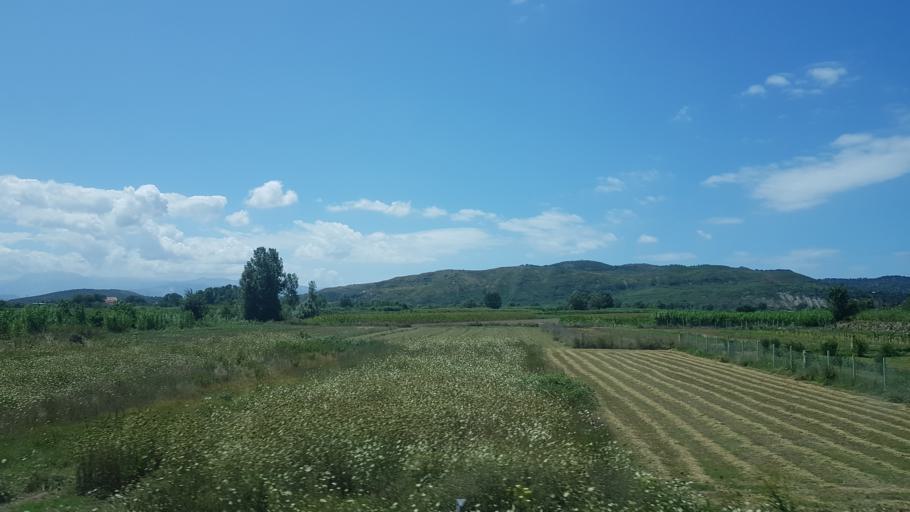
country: AL
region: Fier
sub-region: Rrethi i Fierit
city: Frakulla e Madhe
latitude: 40.6075
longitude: 19.5385
